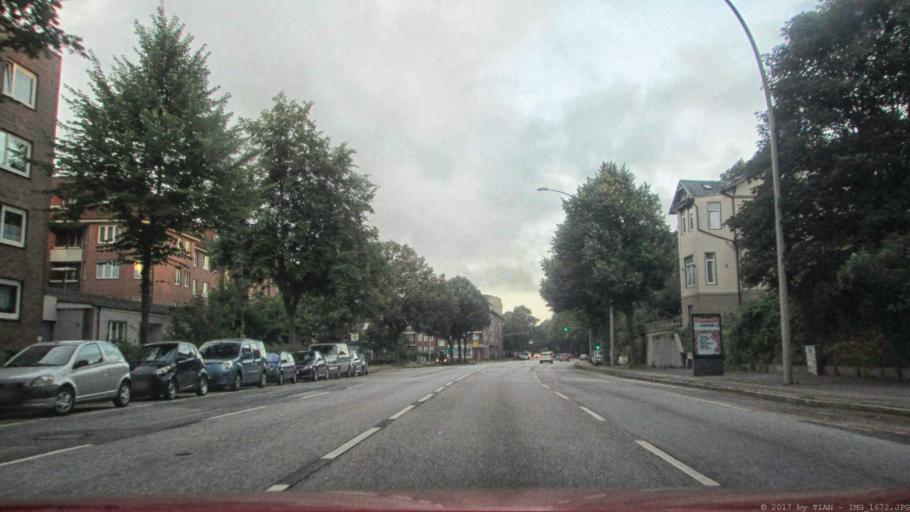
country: DE
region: Hamburg
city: Marienthal
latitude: 53.5451
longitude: 10.0895
